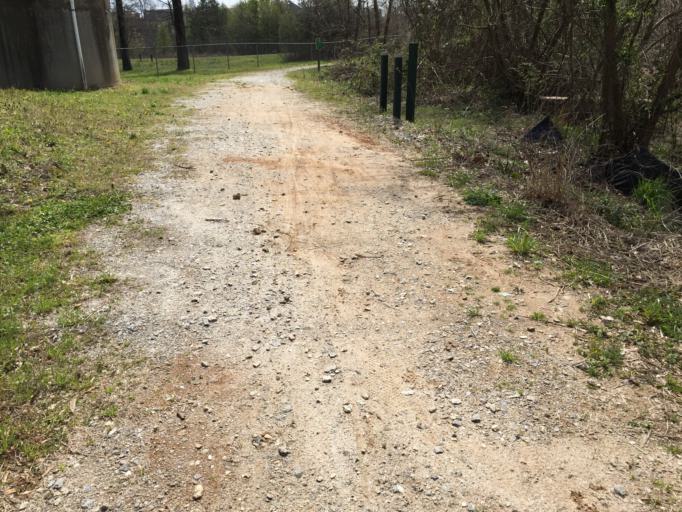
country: US
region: South Carolina
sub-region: Greenville County
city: Mauldin
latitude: 34.7985
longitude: -82.3644
